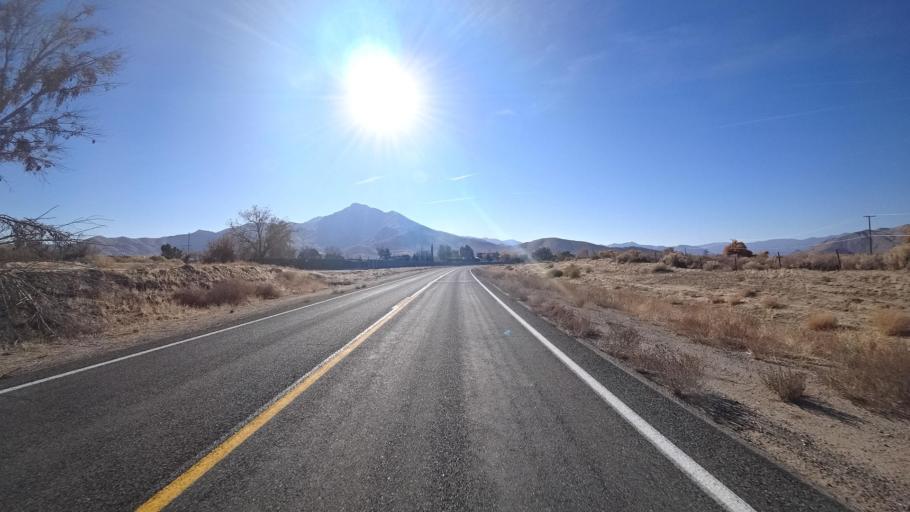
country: US
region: California
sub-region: Kern County
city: Weldon
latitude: 35.6693
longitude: -118.2637
